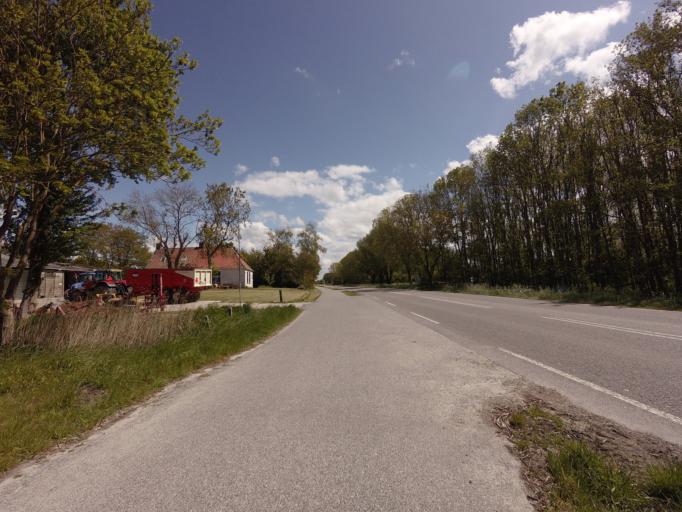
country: NL
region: Friesland
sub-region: Gemeente Harlingen
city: Harlingen
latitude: 53.1372
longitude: 5.4543
